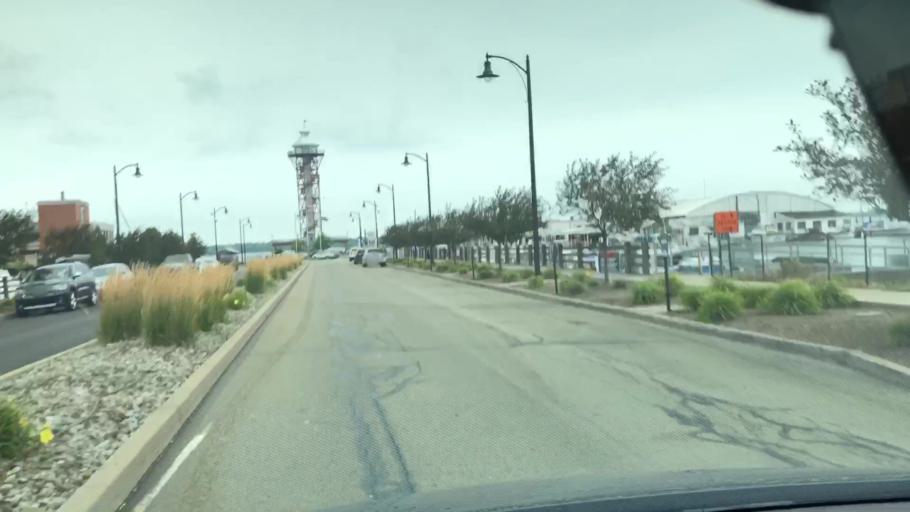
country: US
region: Pennsylvania
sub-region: Erie County
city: Erie
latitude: 42.1358
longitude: -80.0894
